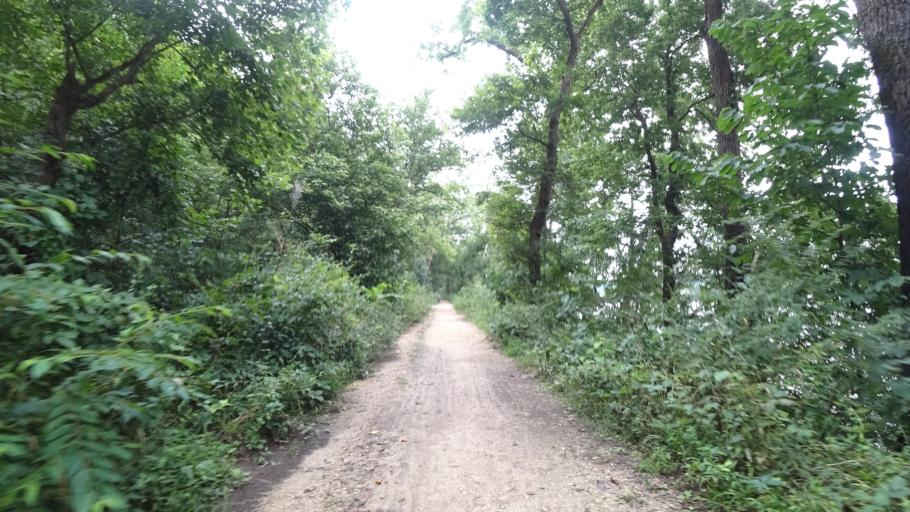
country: US
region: Virginia
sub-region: Loudoun County
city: Lowes Island
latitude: 39.0680
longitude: -77.3582
